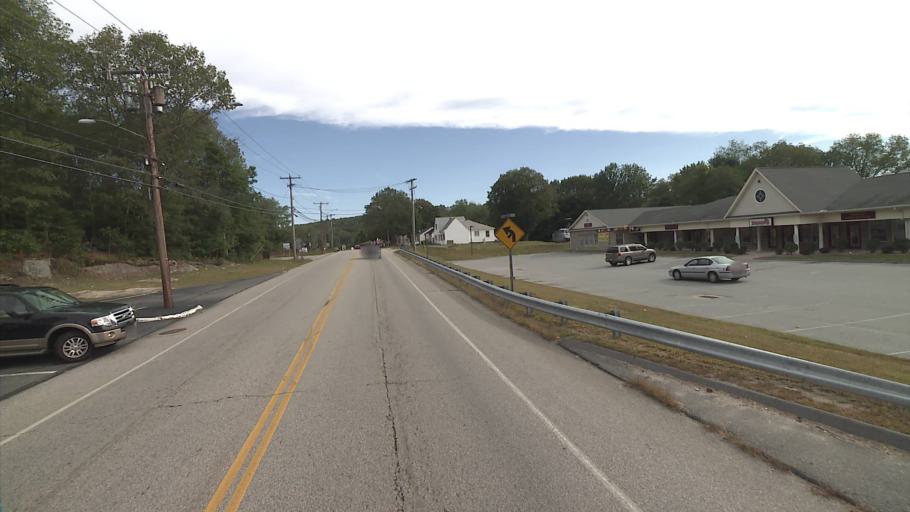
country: US
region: Connecticut
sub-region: New London County
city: Uncasville
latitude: 41.4537
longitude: -72.1065
